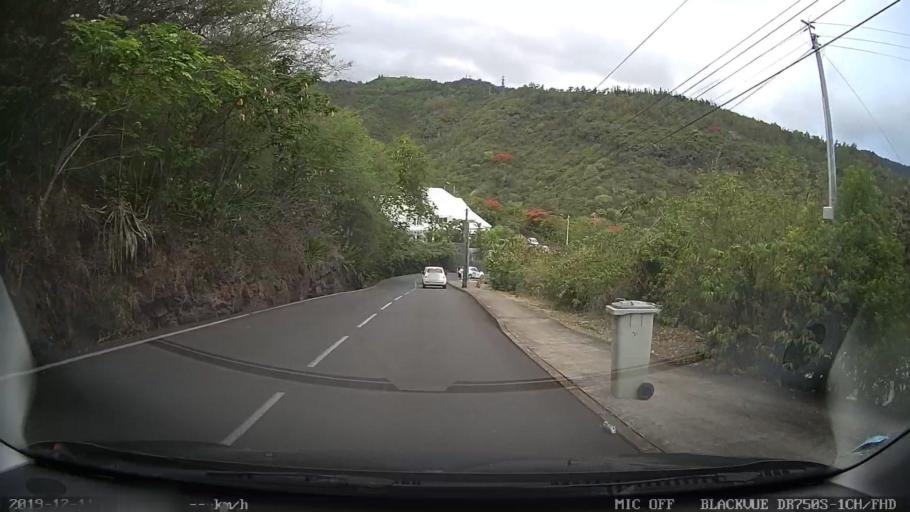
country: RE
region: Reunion
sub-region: Reunion
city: Saint-Denis
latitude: -20.9026
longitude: 55.4573
